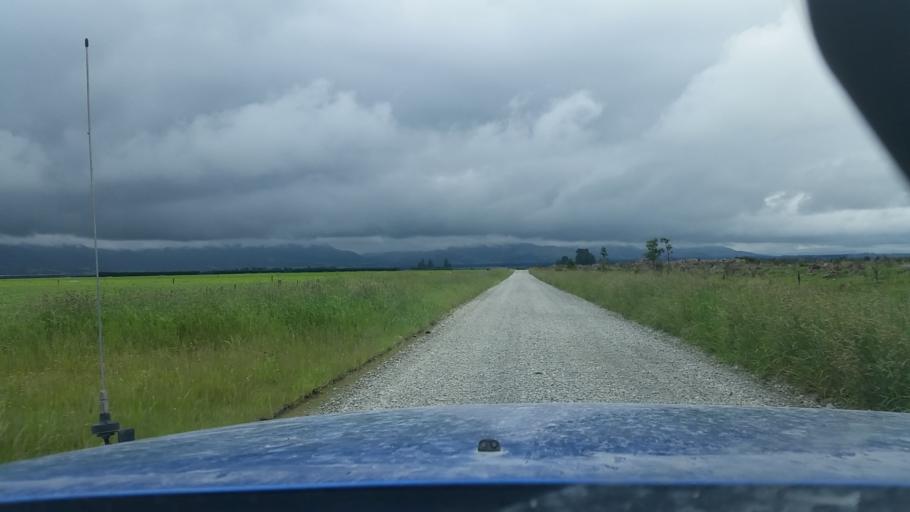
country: NZ
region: Canterbury
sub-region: Ashburton District
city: Methven
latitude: -43.7105
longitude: 171.4589
